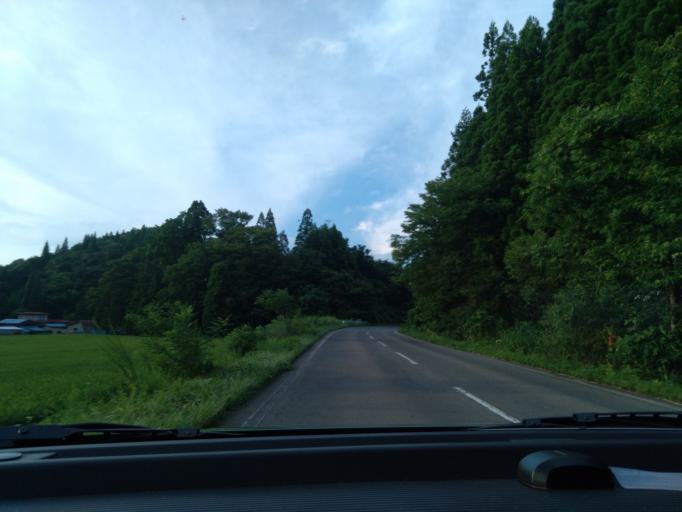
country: JP
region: Akita
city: Akita
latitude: 39.6928
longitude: 140.2282
